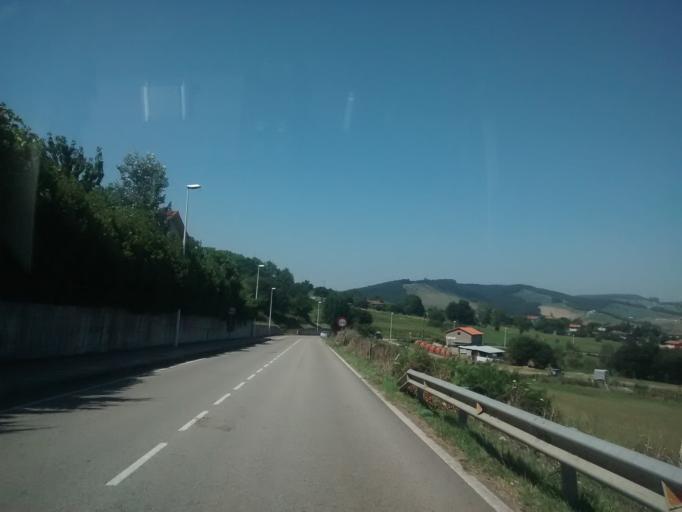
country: ES
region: Cantabria
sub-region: Provincia de Cantabria
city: San Miguel de Meruelo
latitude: 43.4462
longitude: -3.5714
